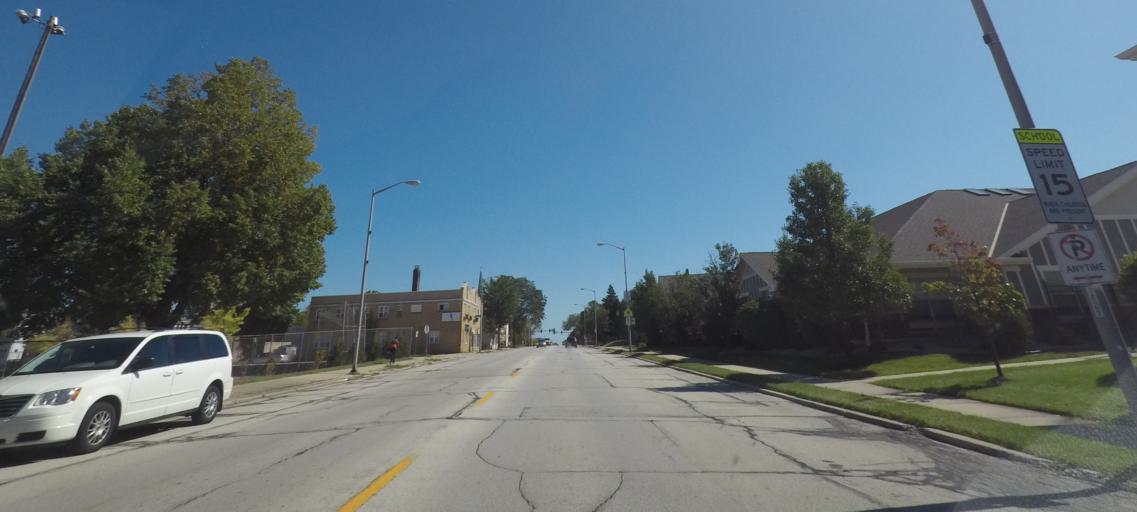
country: US
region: Wisconsin
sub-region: Milwaukee County
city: West Allis
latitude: 43.0112
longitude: -88.0104
